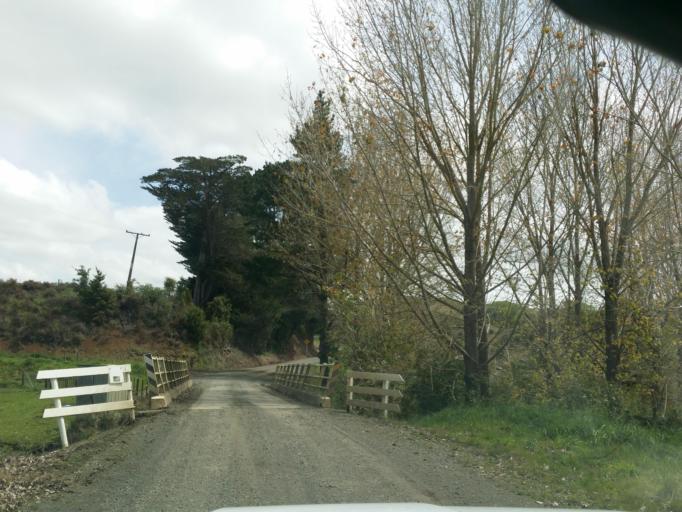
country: NZ
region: Northland
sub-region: Whangarei
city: Maungatapere
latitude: -35.9058
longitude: 174.1290
